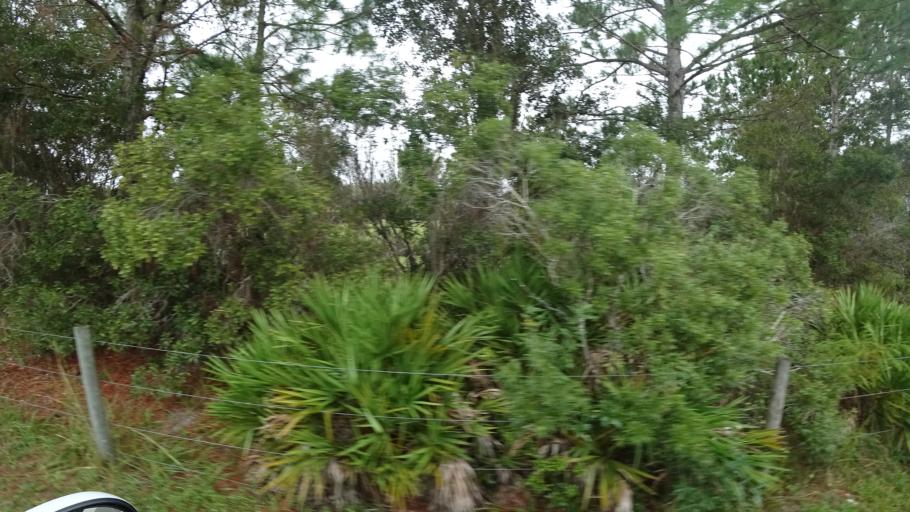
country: US
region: Florida
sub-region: Sarasota County
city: Warm Mineral Springs
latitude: 27.2764
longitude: -82.1327
